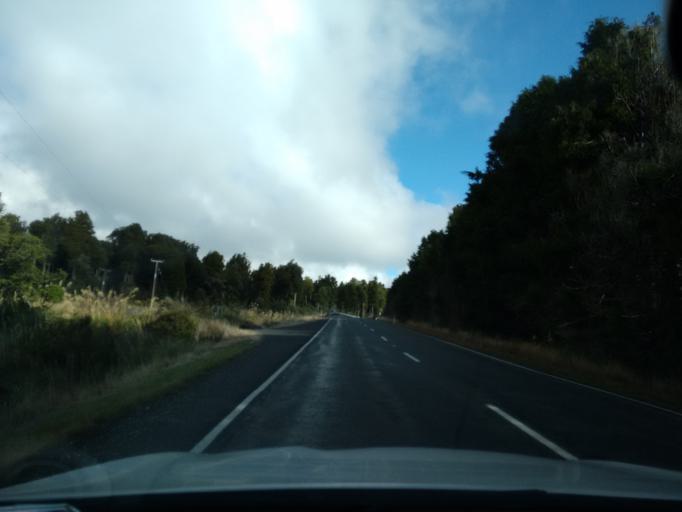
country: NZ
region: Manawatu-Wanganui
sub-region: Ruapehu District
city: Waiouru
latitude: -39.2409
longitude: 175.3917
